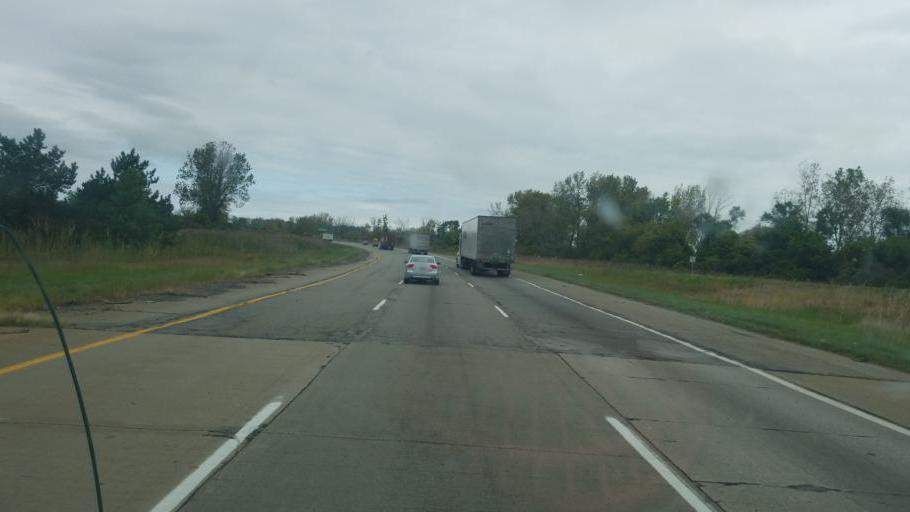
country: US
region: Michigan
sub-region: Monroe County
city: Luna Pier
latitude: 41.7549
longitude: -83.4816
